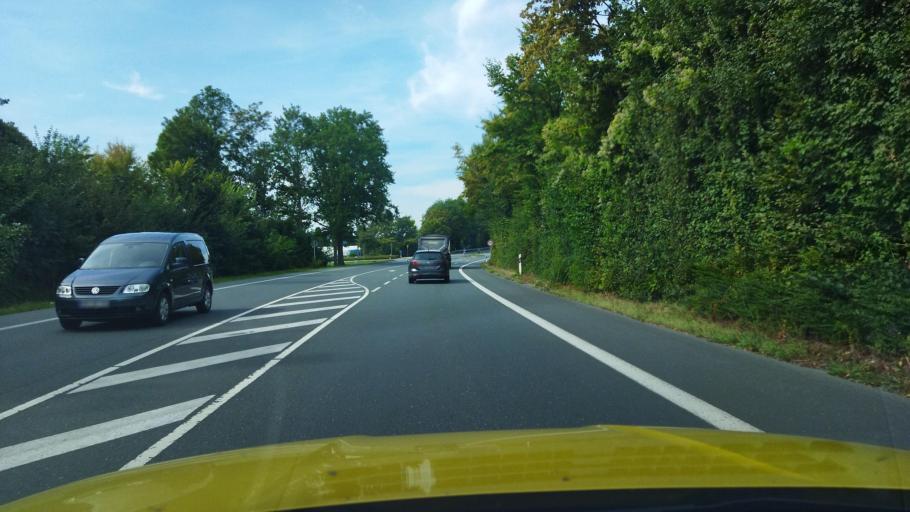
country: DE
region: North Rhine-Westphalia
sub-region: Regierungsbezirk Munster
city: Ennigerloh
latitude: 51.7949
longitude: 8.0161
